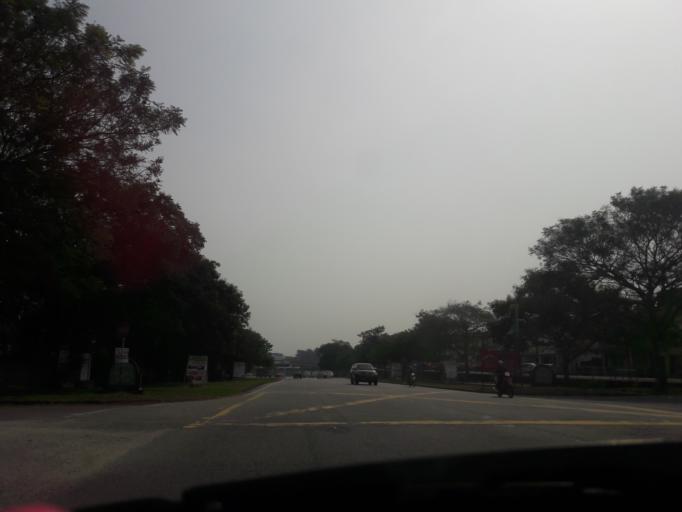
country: MY
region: Kedah
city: Kulim
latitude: 5.3803
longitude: 100.5440
